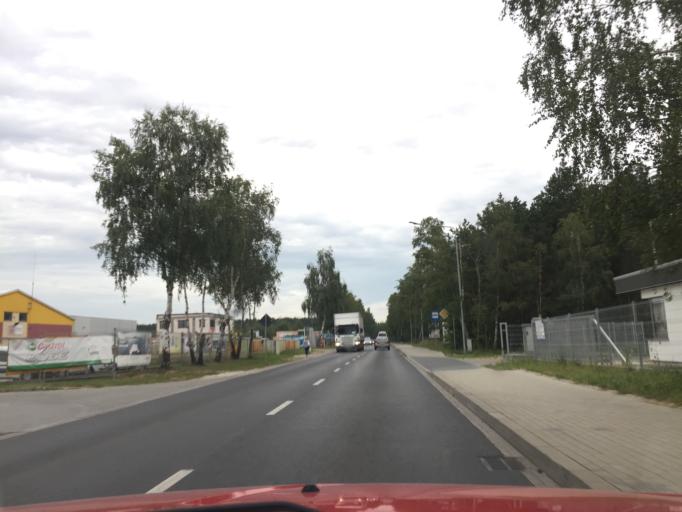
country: PL
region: Greater Poland Voivodeship
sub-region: Powiat poznanski
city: Baranowo
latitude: 52.4078
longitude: 16.7938
